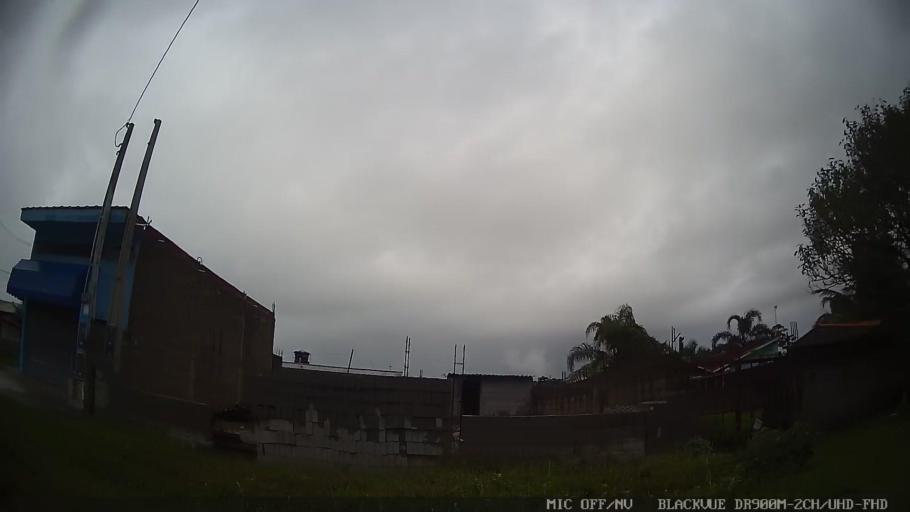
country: BR
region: Sao Paulo
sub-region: Peruibe
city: Peruibe
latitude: -24.2512
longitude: -46.9000
